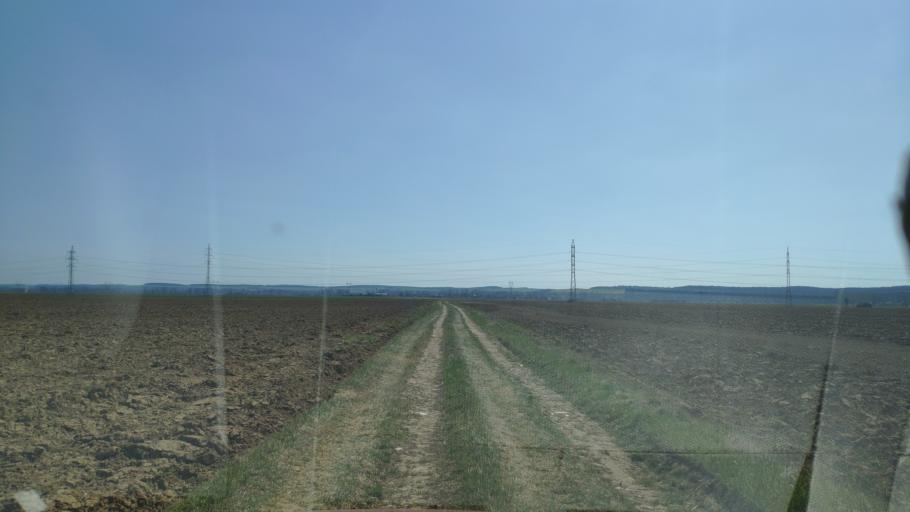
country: SK
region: Kosicky
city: Moldava nad Bodvou
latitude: 48.6014
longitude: 20.9446
